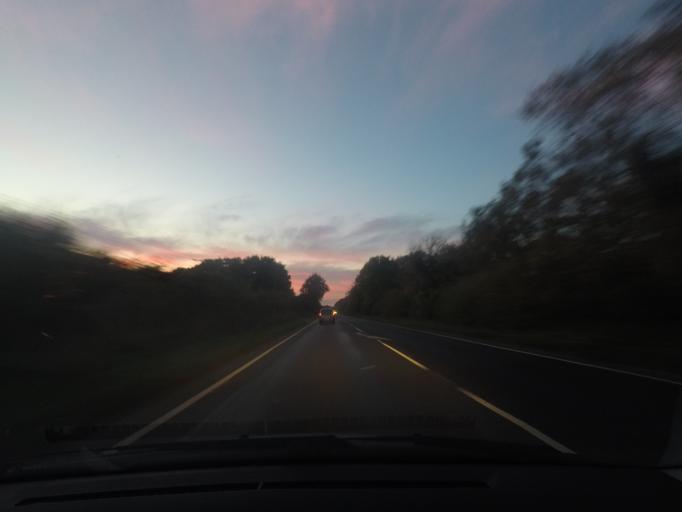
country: GB
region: England
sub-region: East Riding of Yorkshire
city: Pocklington
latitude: 53.9218
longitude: -0.8005
